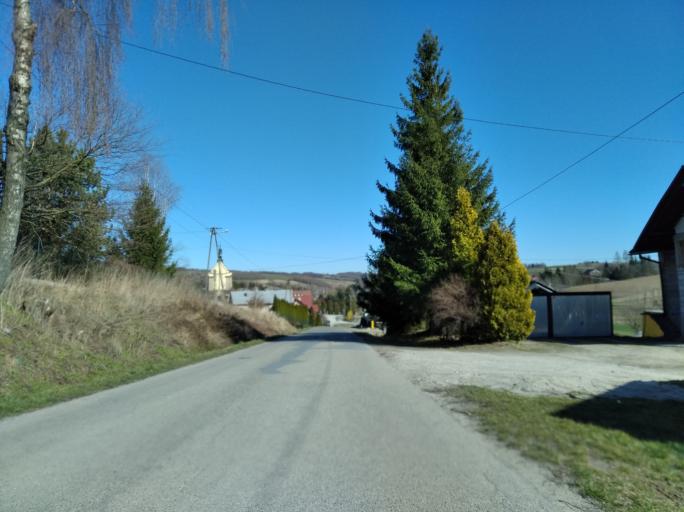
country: PL
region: Subcarpathian Voivodeship
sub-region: Powiat strzyzowski
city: Wisniowa
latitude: 49.9140
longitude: 21.7051
